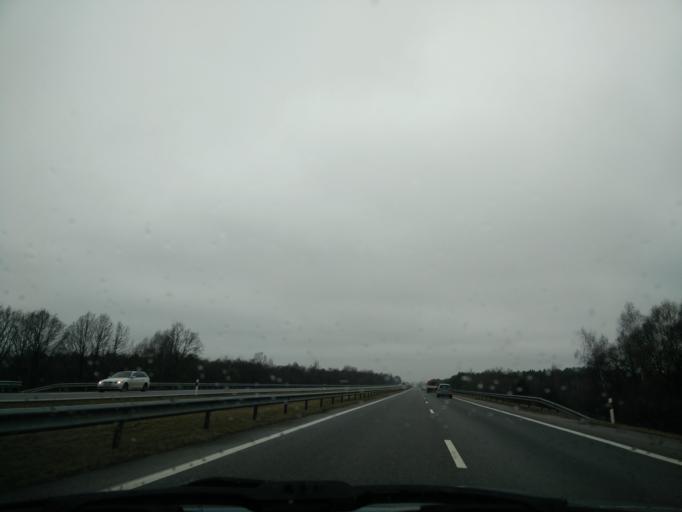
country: LT
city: Raseiniai
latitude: 55.3937
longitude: 22.8767
